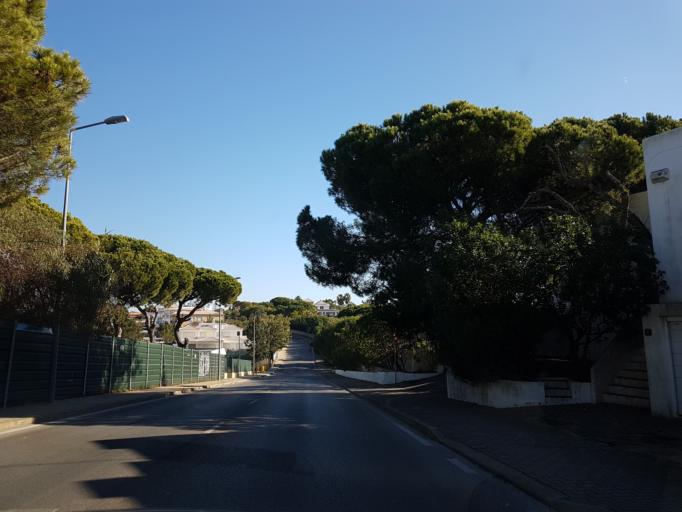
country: PT
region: Faro
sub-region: Albufeira
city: Albufeira
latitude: 37.0929
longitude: -8.2034
